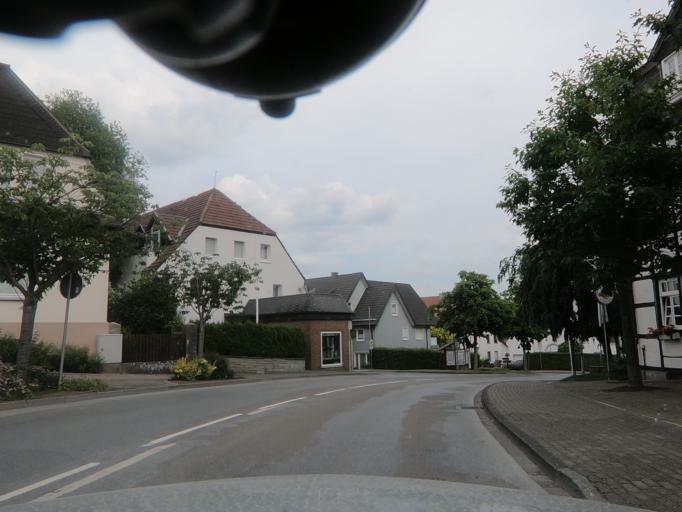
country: DE
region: North Rhine-Westphalia
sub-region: Regierungsbezirk Arnsberg
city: Ruthen
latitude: 51.4521
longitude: 8.4233
